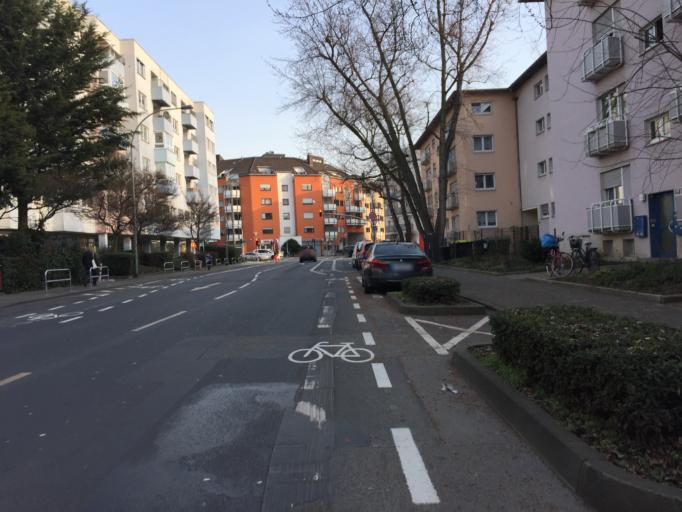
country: DE
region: Hesse
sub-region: Regierungsbezirk Darmstadt
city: Frankfurt am Main
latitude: 50.1381
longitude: 8.6663
